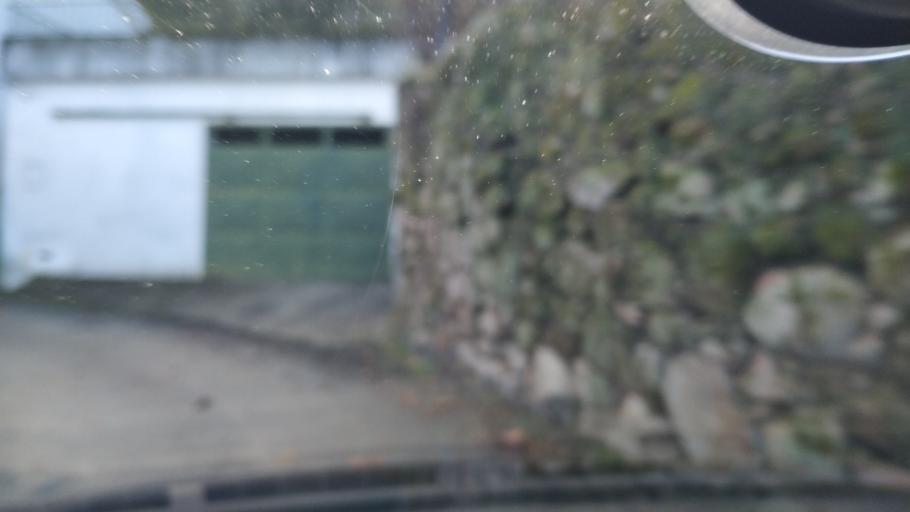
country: PT
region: Vila Real
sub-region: Santa Marta de Penaguiao
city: Santa Marta de Penaguiao
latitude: 41.2527
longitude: -7.7740
